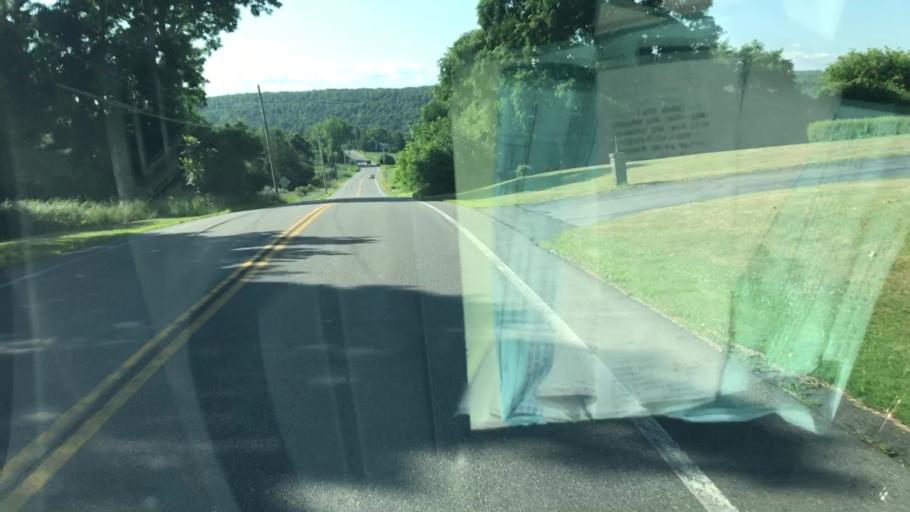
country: US
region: New York
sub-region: Onondaga County
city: Marcellus
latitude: 43.0331
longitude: -76.3650
